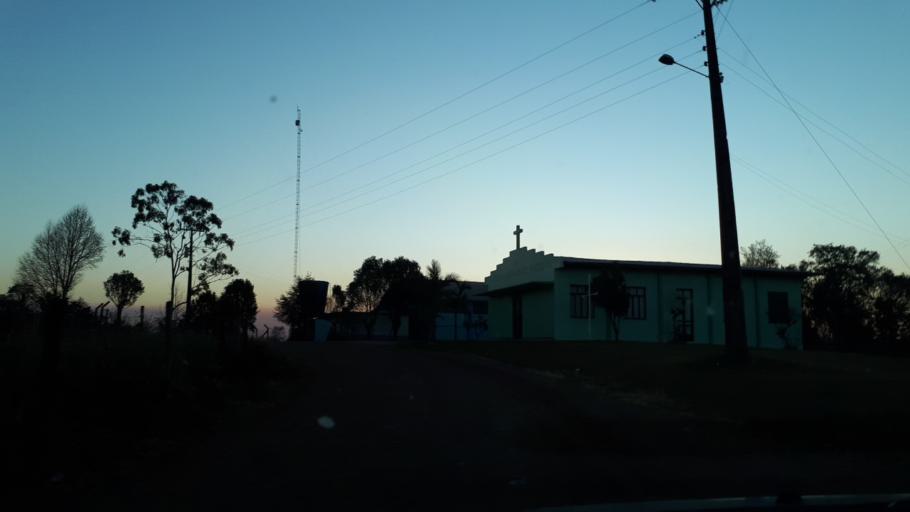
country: AR
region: Misiones
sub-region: Departamento de San Pedro
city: San Pedro
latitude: -26.8302
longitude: -53.6256
